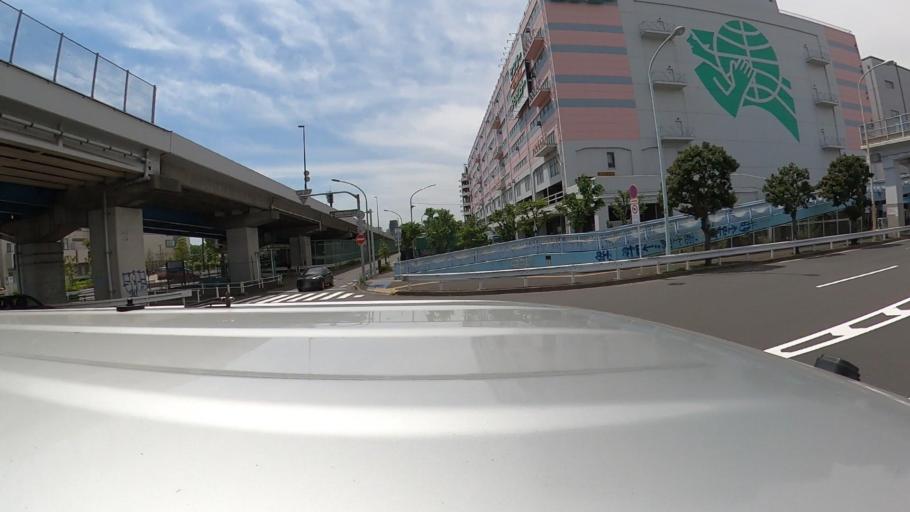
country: JP
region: Kanagawa
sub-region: Kawasaki-shi
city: Kawasaki
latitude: 35.5843
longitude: 139.7433
